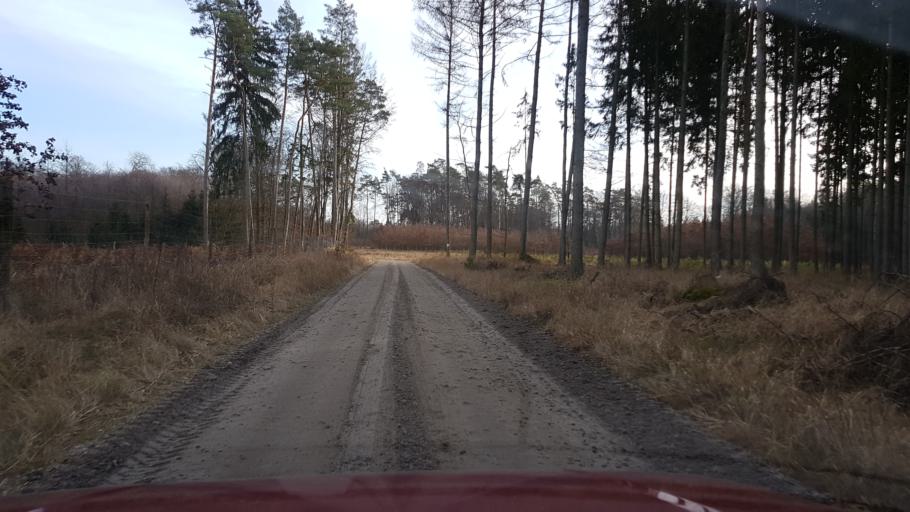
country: PL
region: West Pomeranian Voivodeship
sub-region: Powiat choszczenski
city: Pelczyce
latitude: 52.9134
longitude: 15.3742
